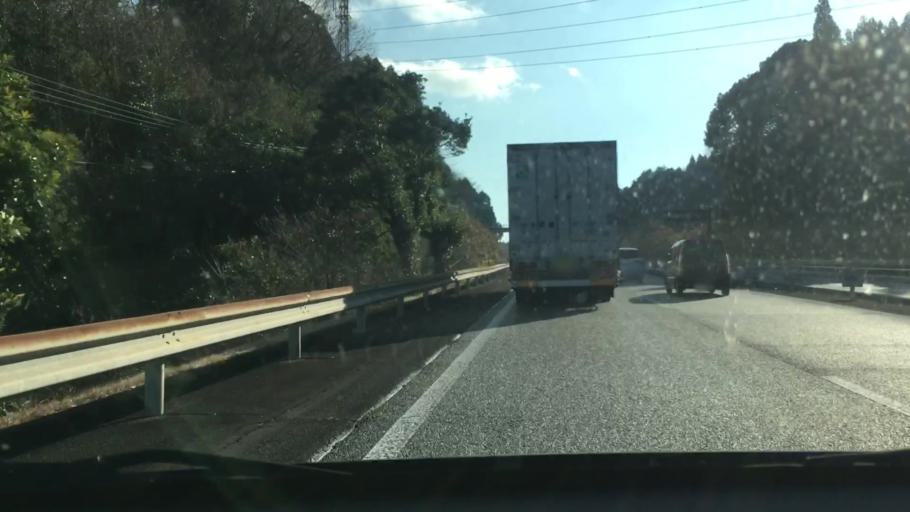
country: JP
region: Kagoshima
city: Okuchi-shinohara
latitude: 31.9306
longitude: 130.7054
